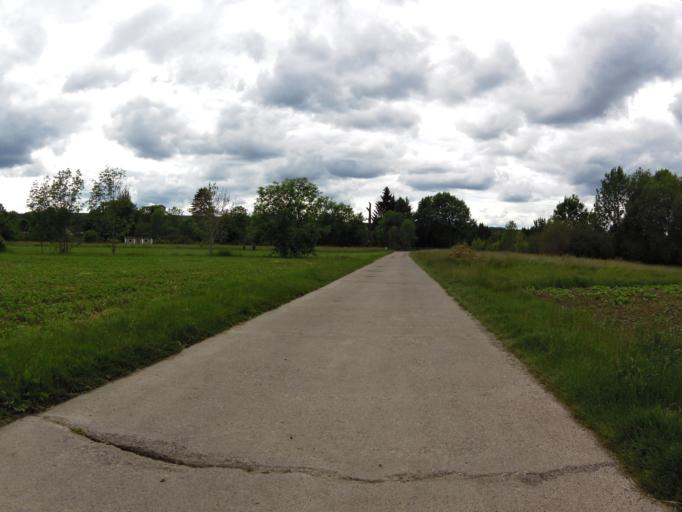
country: DE
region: Thuringia
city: Oberdorla
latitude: 51.1624
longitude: 10.4144
